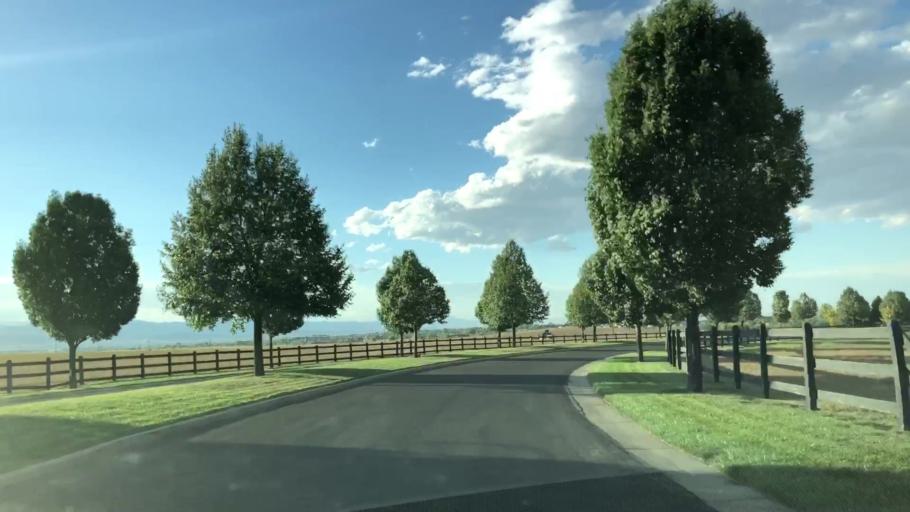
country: US
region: Colorado
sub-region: Larimer County
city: Loveland
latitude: 40.4775
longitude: -105.0078
